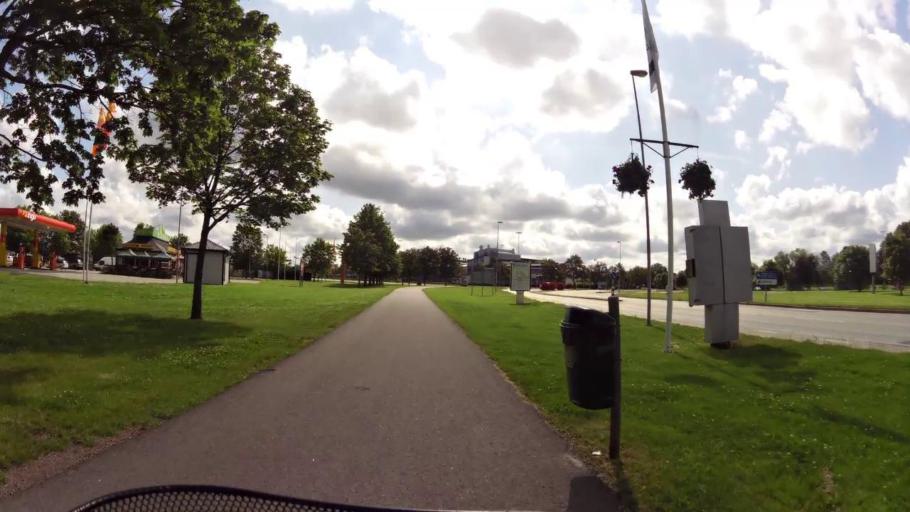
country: SE
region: OEstergoetland
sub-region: Linkopings Kommun
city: Linkoping
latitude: 58.4162
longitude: 15.6376
